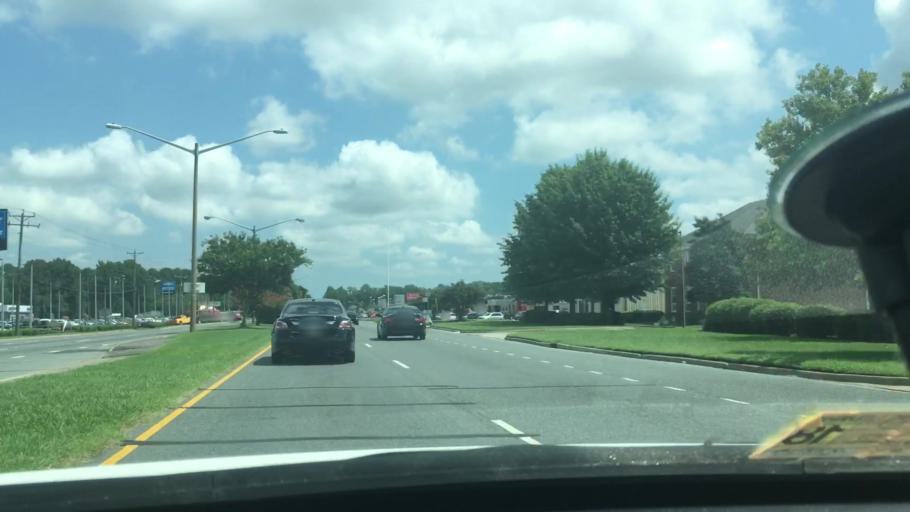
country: US
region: Virginia
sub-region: City of Chesapeake
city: Chesapeake
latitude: 36.7975
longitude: -76.2344
